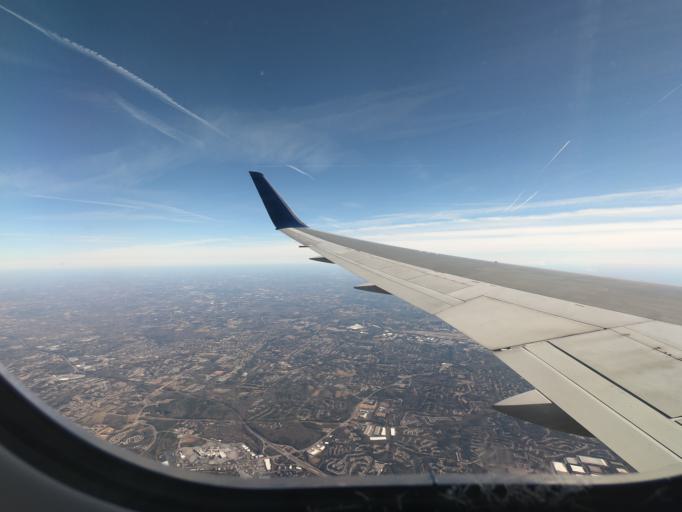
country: US
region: Georgia
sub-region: Gwinnett County
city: Sugar Hill
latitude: 34.0838
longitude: -84.0432
